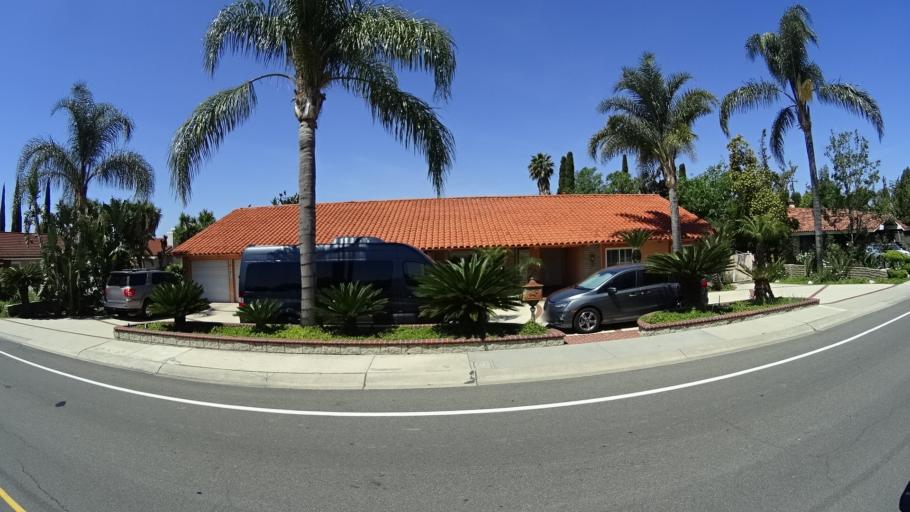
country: US
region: California
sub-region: Orange County
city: Villa Park
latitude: 33.8156
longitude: -117.8134
